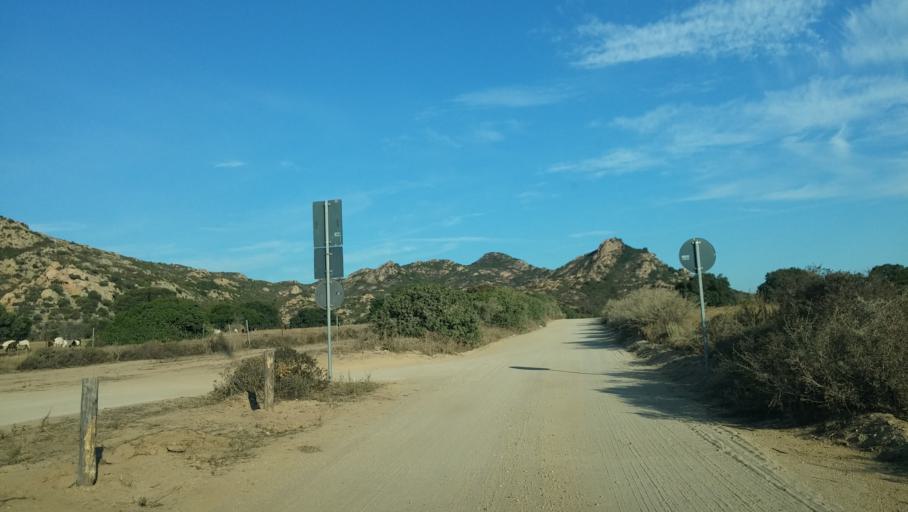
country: IT
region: Sardinia
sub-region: Provincia di Nuoro
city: La Caletta
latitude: 40.4816
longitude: 9.8053
